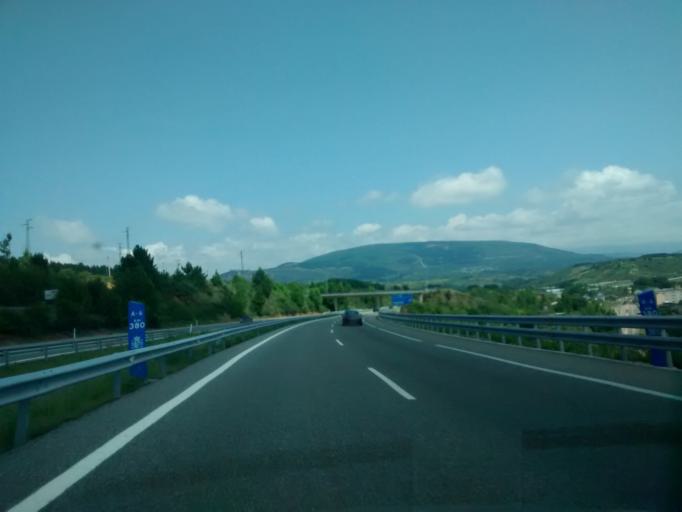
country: ES
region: Castille and Leon
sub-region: Provincia de Leon
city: Congosto
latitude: 42.5821
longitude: -6.5290
